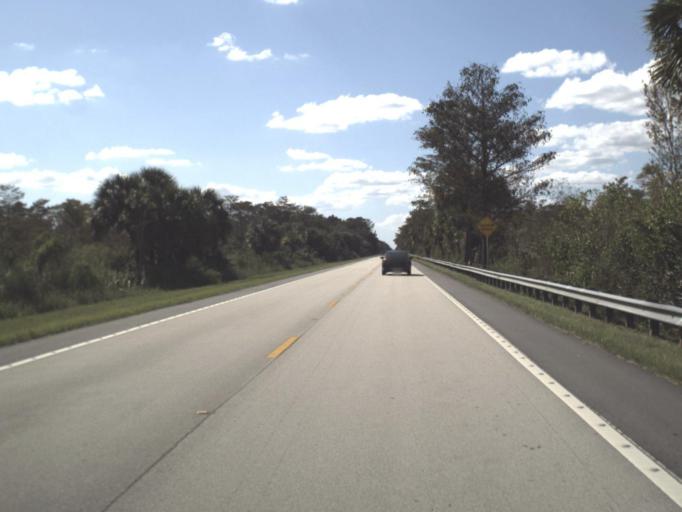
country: US
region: Florida
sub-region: Collier County
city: Marco
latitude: 25.8714
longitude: -81.1759
